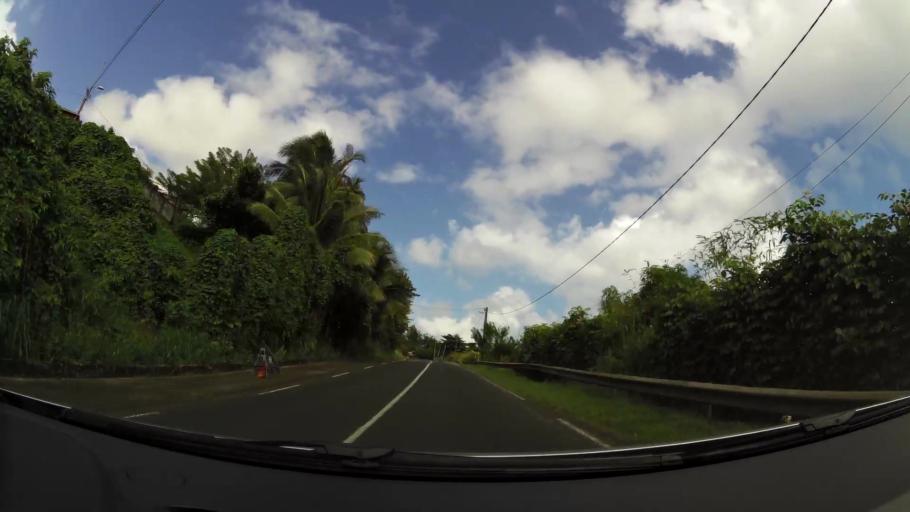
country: MQ
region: Martinique
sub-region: Martinique
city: Le Lorrain
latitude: 14.8132
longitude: -61.0219
